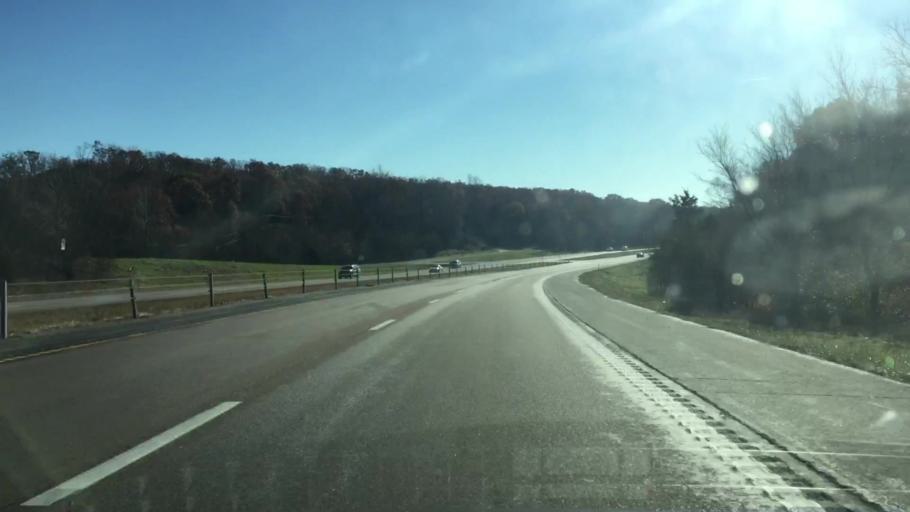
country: US
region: Missouri
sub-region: Cole County
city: Jefferson City
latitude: 38.6687
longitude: -92.2308
